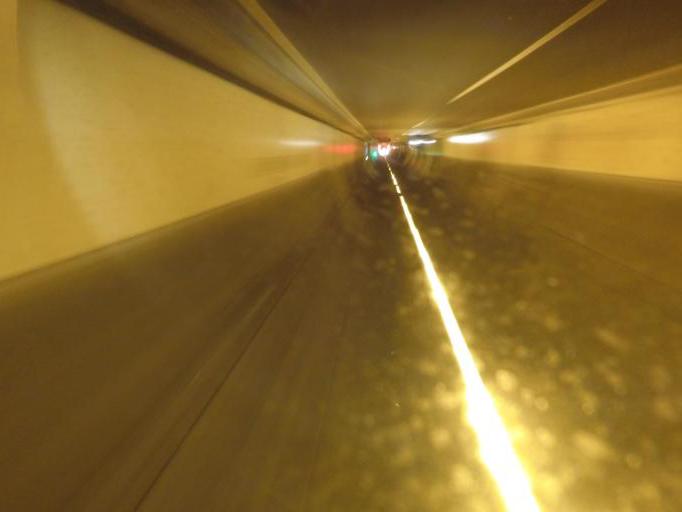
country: PT
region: Madeira
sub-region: Calheta
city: Estreito da Calheta
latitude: 32.7314
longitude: -17.1832
